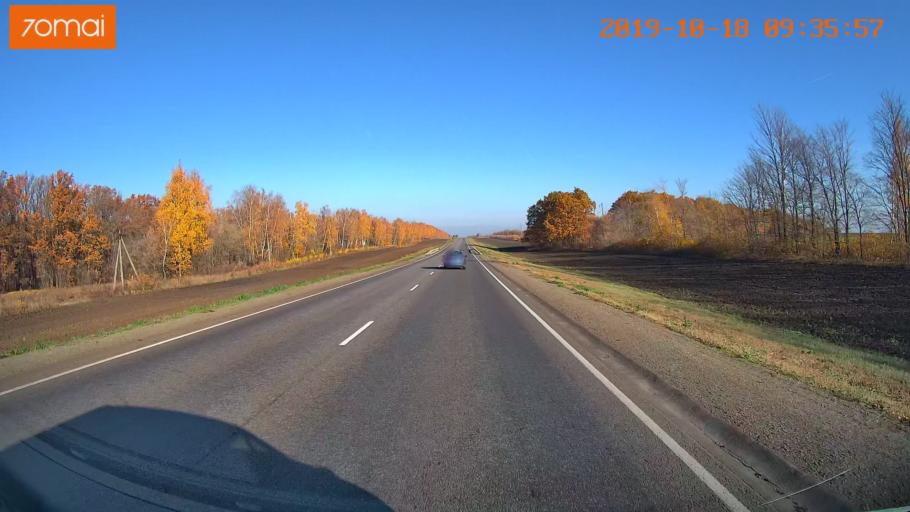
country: RU
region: Tula
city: Yefremov
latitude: 53.1991
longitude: 38.1469
